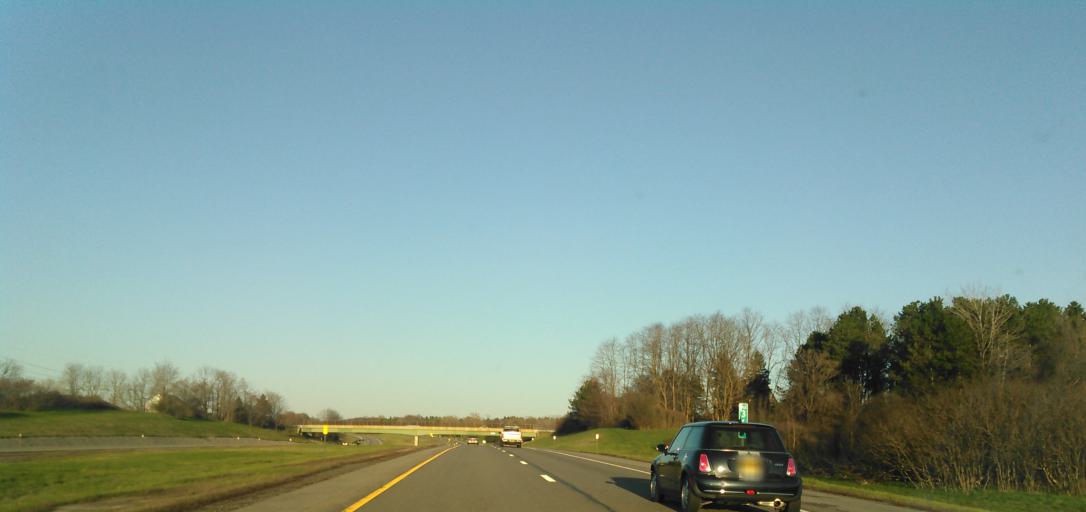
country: US
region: New York
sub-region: Monroe County
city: Honeoye Falls
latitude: 43.0477
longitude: -77.6235
